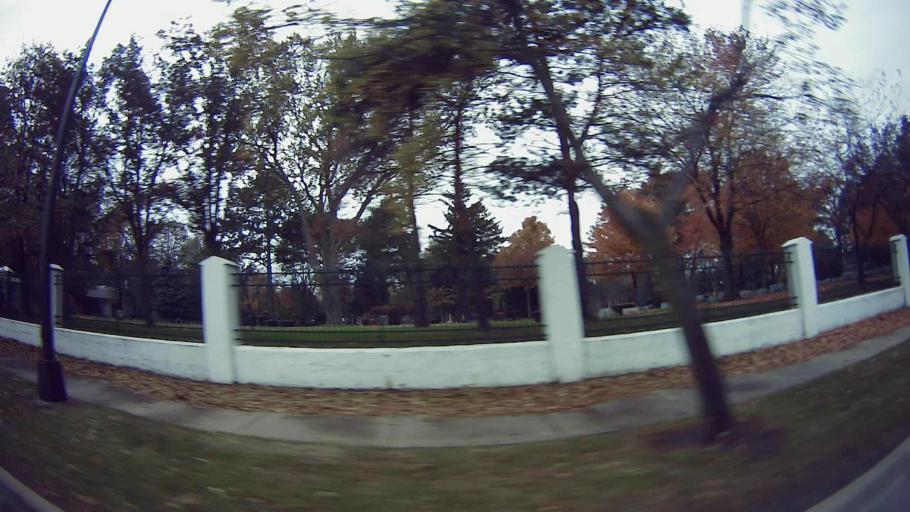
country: US
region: Michigan
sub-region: Oakland County
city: Ferndale
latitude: 42.4529
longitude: -83.1296
